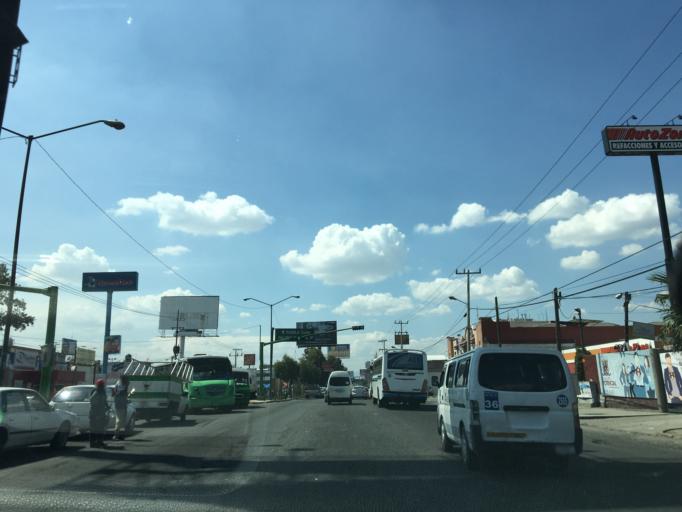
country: MX
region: Mexico
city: Los Reyes La Paz
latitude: 19.3567
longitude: -98.9849
